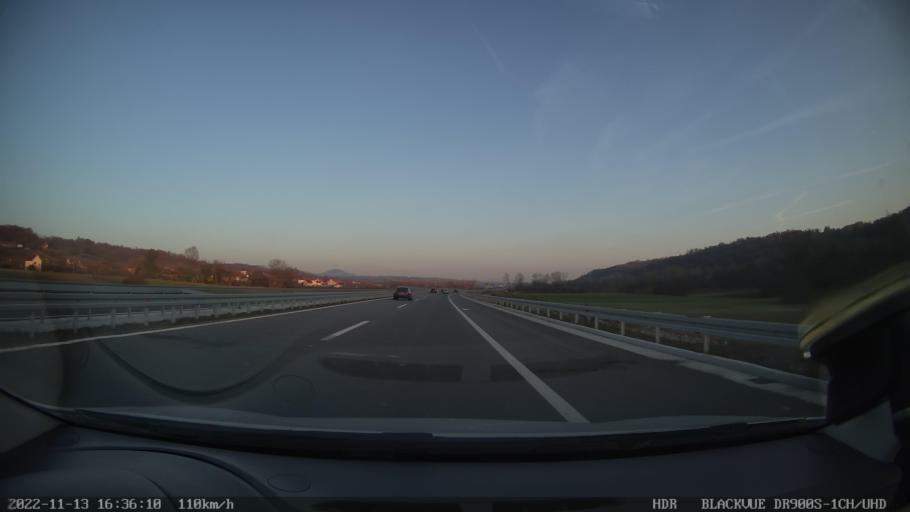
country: RS
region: Central Serbia
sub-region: Moravicki Okrug
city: Cacak
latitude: 43.9228
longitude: 20.3721
